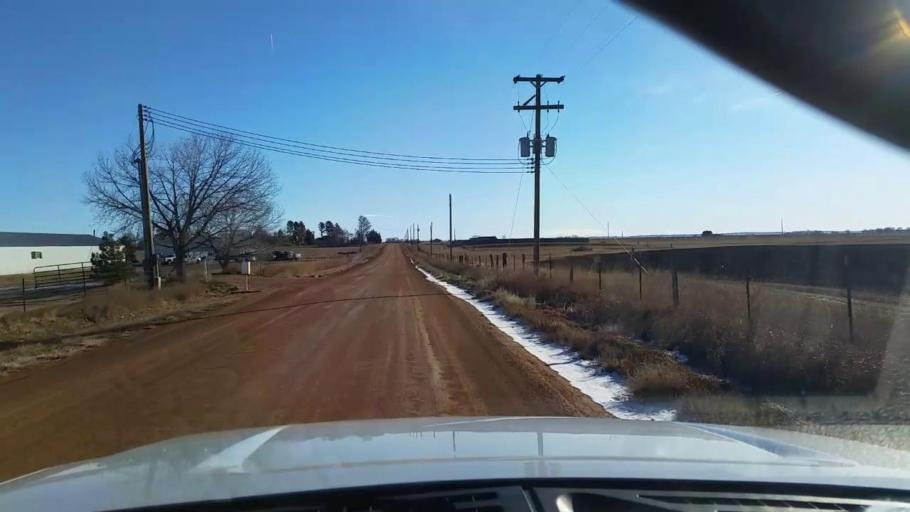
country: US
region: Colorado
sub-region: Larimer County
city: Wellington
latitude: 40.7695
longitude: -105.0708
